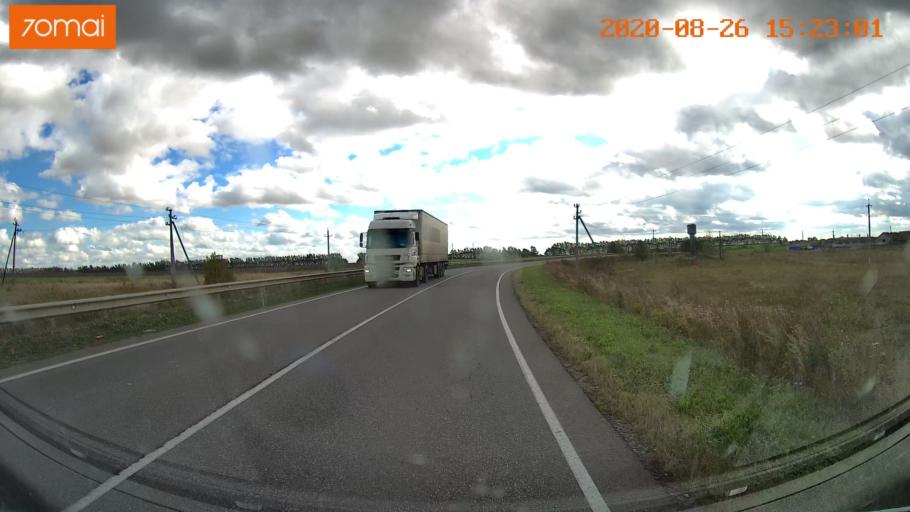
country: RU
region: Tula
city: Severo-Zadonsk
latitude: 54.1230
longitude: 38.4556
